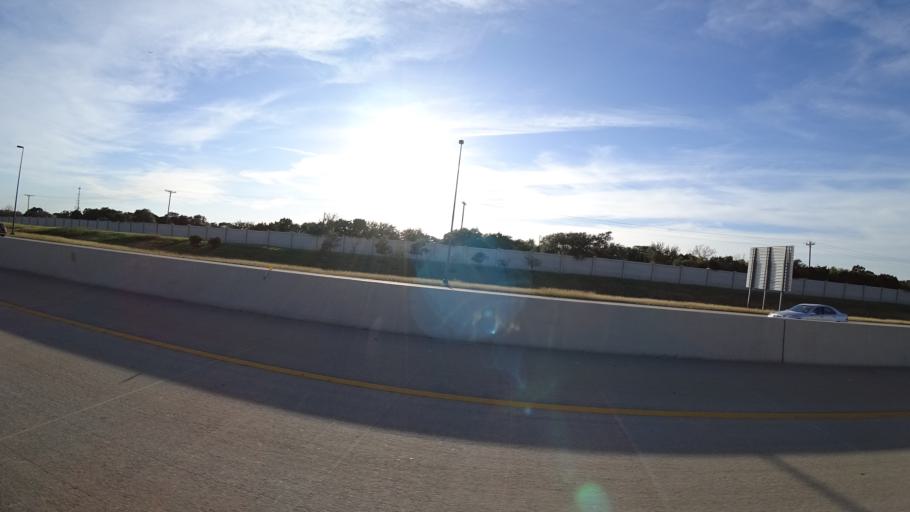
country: US
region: Texas
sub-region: Williamson County
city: Cedar Park
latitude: 30.5090
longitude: -97.8113
